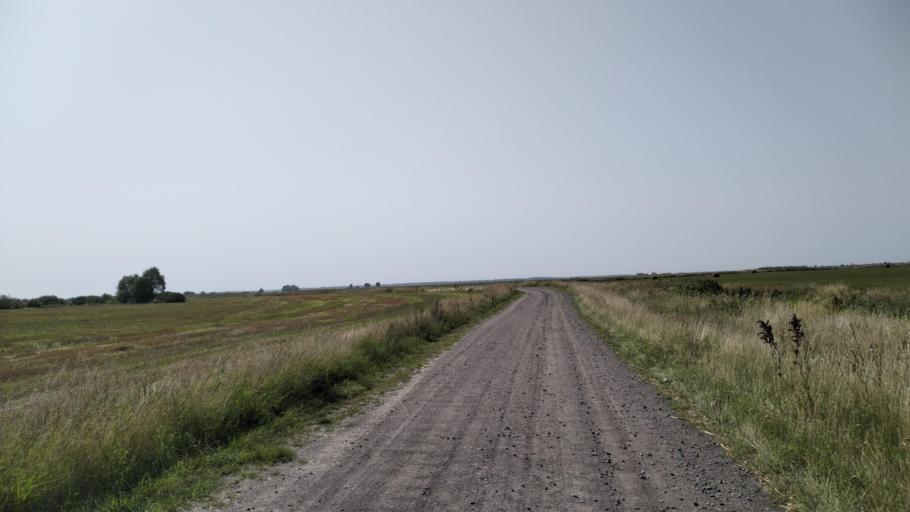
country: BY
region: Brest
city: Davyd-Haradok
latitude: 52.0115
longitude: 27.1662
